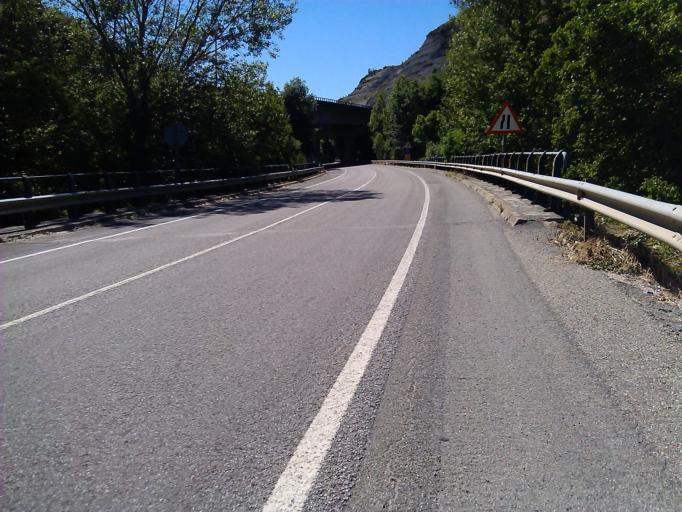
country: ES
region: Castille and Leon
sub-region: Provincia de Leon
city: Trabadelo
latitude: 42.6552
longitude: -6.8926
